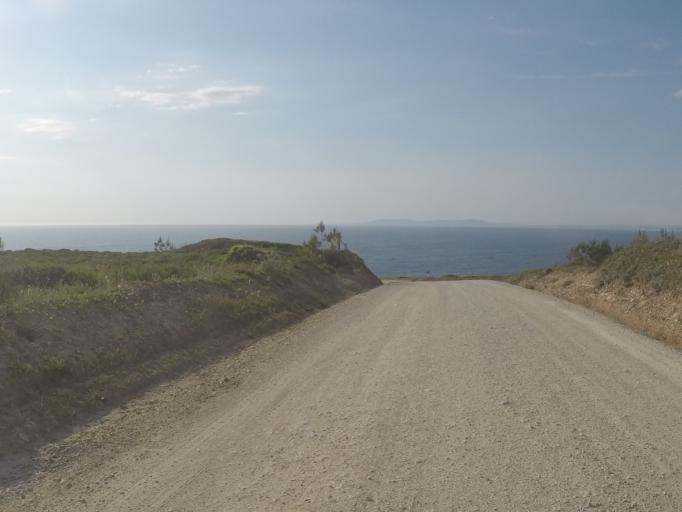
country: PT
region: Setubal
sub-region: Sesimbra
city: Sesimbra
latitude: 38.4485
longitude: -9.2000
